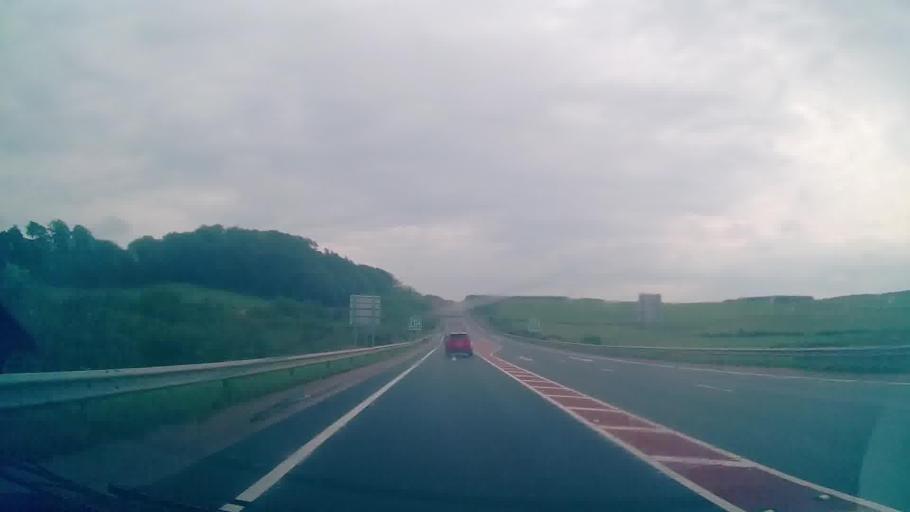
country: GB
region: Scotland
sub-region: Dumfries and Galloway
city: Lockerbie
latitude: 55.0270
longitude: -3.3860
